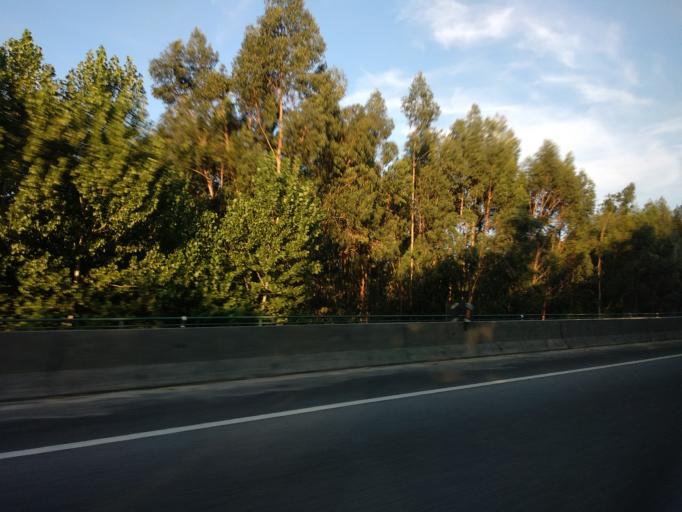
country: PT
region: Braga
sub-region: Vila Verde
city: Prado
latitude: 41.6017
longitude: -8.4483
